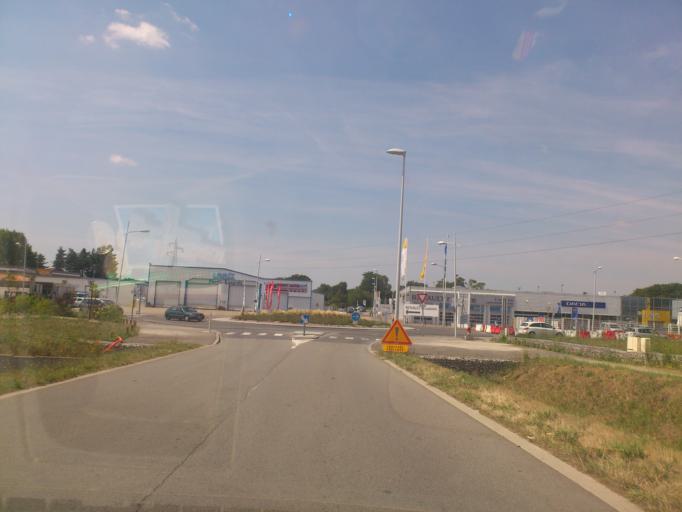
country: FR
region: Pays de la Loire
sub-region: Departement de la Loire-Atlantique
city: Les Sorinieres
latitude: 47.1556
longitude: -1.5369
